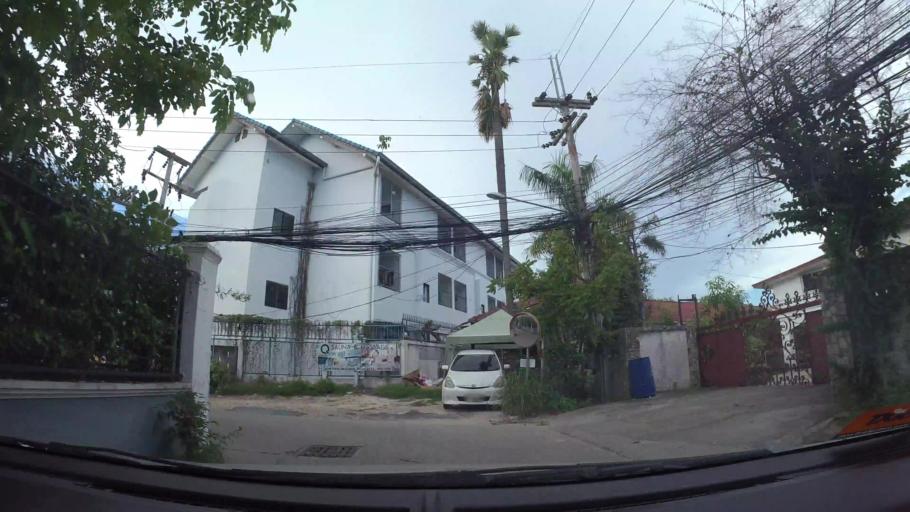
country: TH
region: Chon Buri
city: Phatthaya
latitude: 12.9166
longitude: 100.8776
